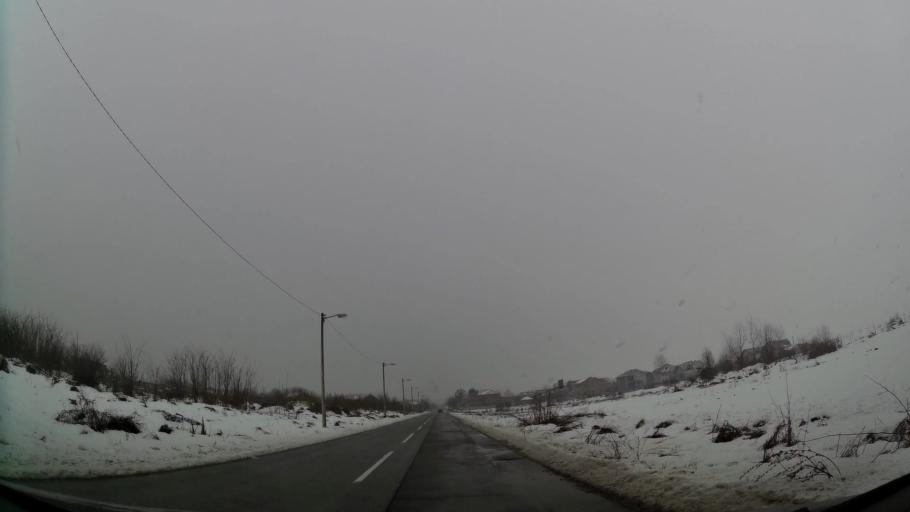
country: RS
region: Central Serbia
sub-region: Belgrade
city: Zemun
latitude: 44.8545
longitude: 20.3324
